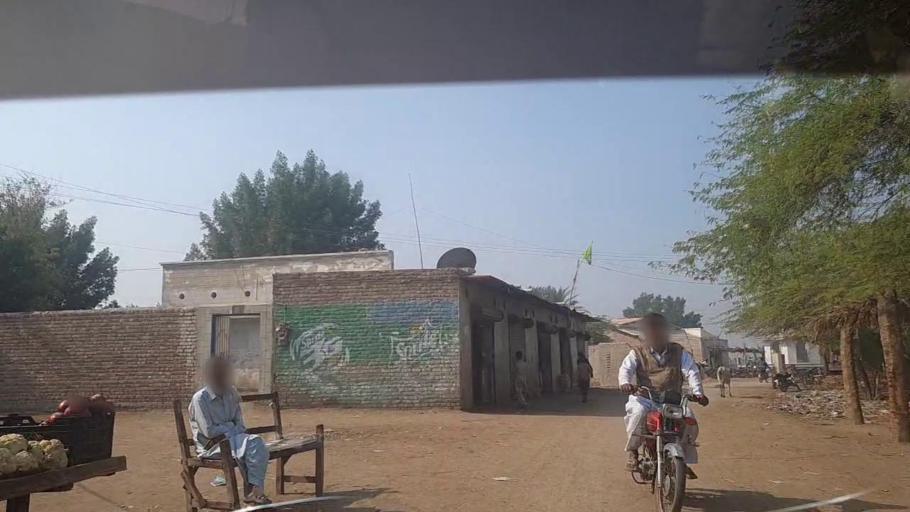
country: PK
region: Sindh
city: Khairpur
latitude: 27.4708
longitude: 68.7099
